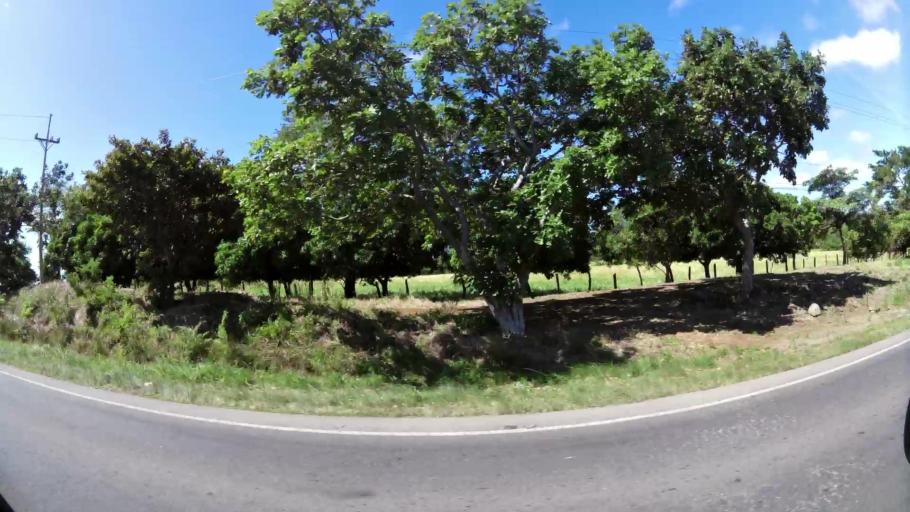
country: CR
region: Guanacaste
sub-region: Canton de Canas
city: Canas
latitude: 10.3959
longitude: -85.0803
